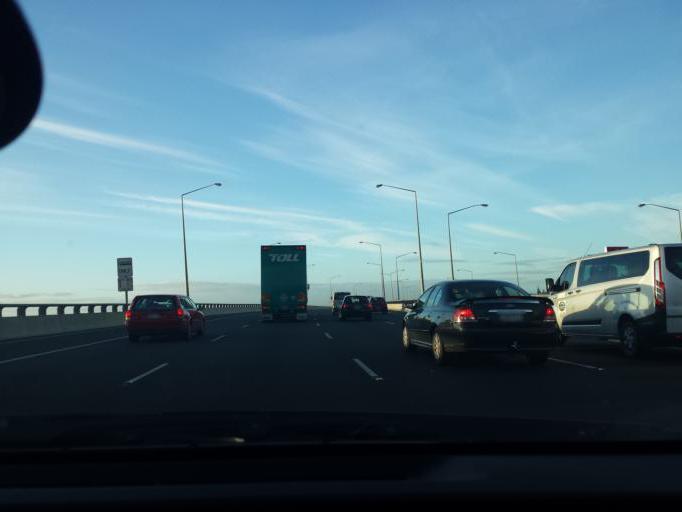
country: NZ
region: Auckland
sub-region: Auckland
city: Mangere
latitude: -36.9324
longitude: 174.7879
